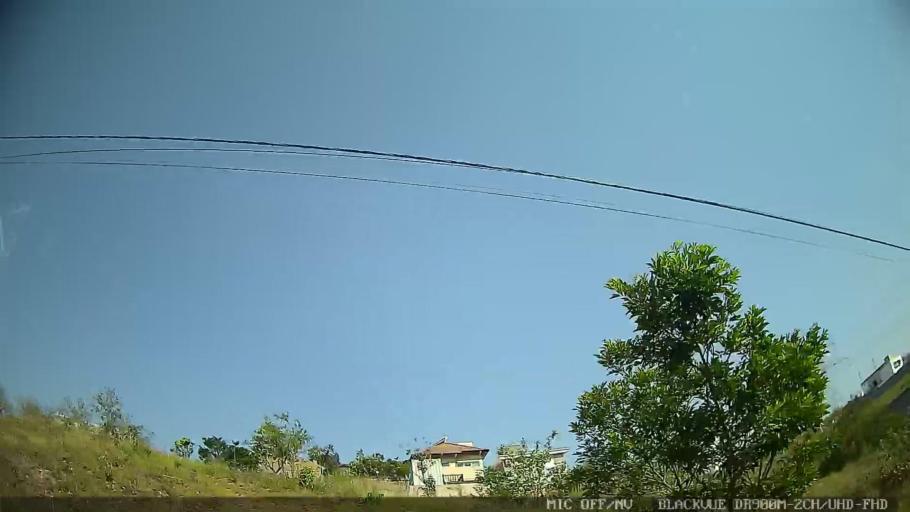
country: BR
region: Sao Paulo
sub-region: Itatiba
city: Itatiba
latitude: -23.0184
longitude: -46.8577
